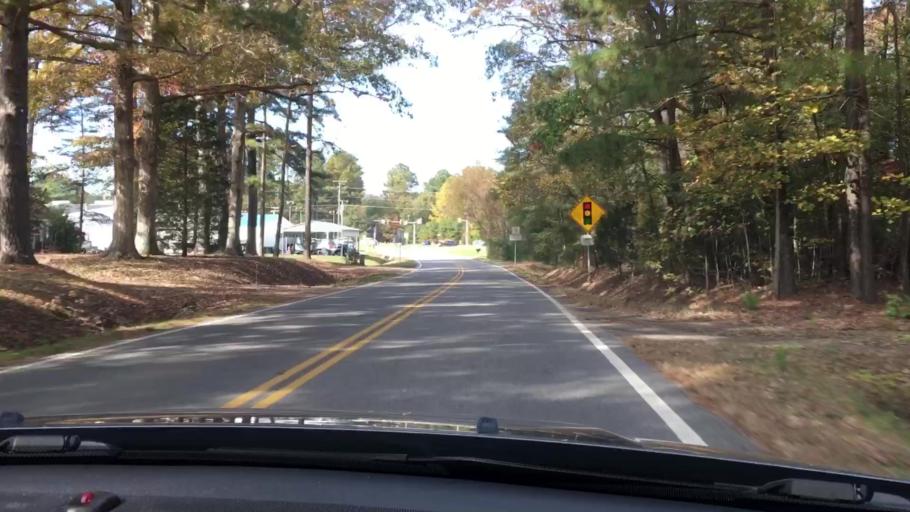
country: US
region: Virginia
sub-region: King William County
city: West Point
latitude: 37.5224
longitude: -76.8249
